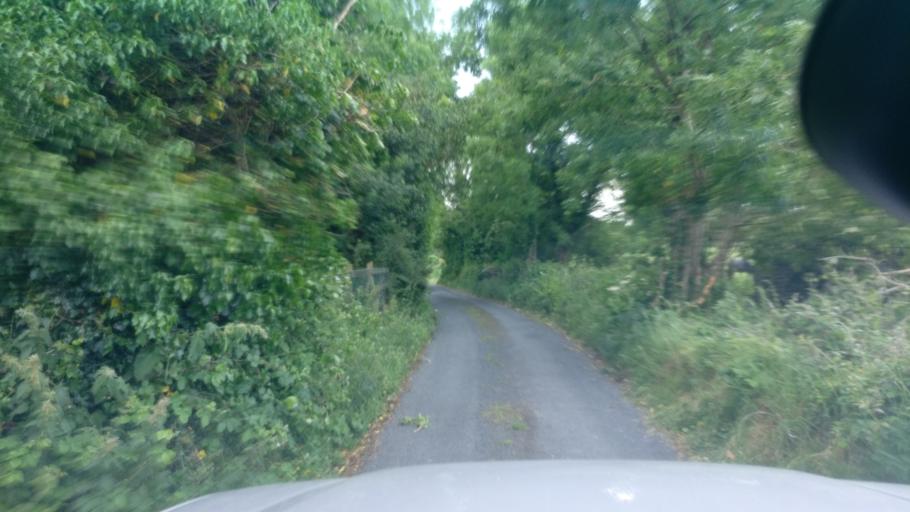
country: IE
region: Connaught
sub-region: County Galway
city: Ballinasloe
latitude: 53.3062
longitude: -8.2767
